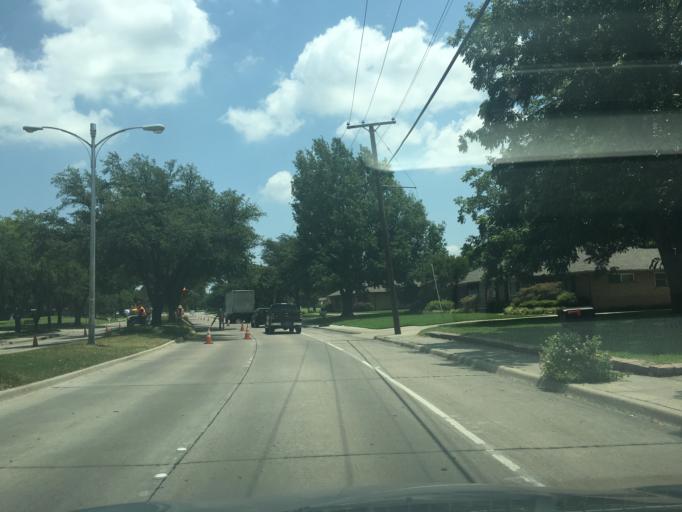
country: US
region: Texas
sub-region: Dallas County
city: Farmers Branch
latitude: 32.9322
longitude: -96.8621
